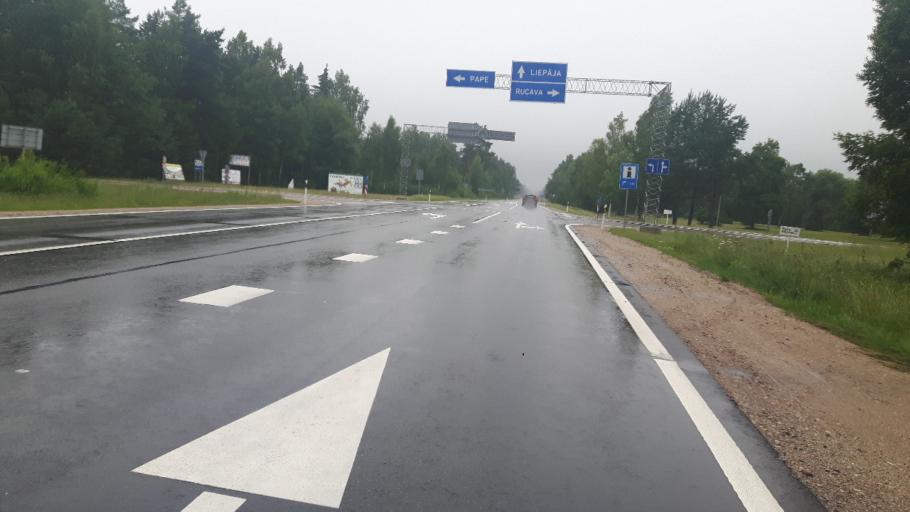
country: LV
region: Rucavas
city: Rucava
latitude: 56.1569
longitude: 21.1476
